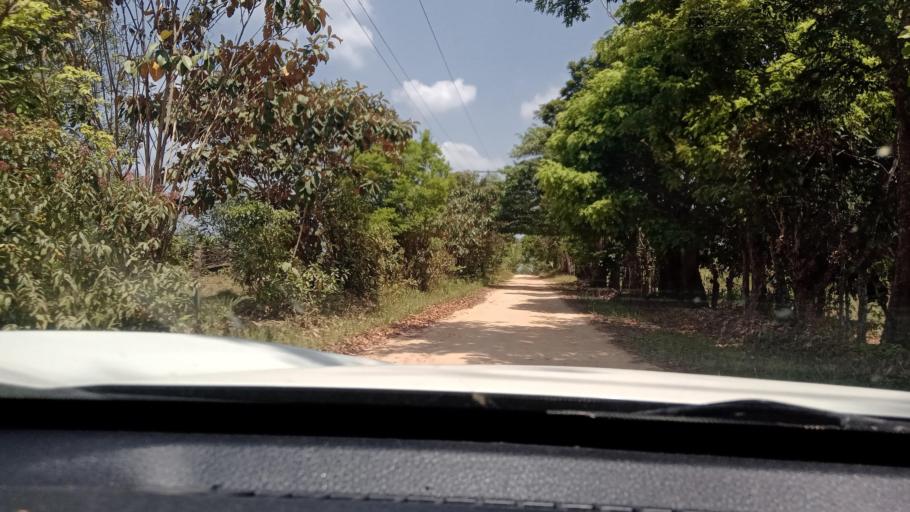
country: MX
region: Veracruz
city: Las Choapas
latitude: 17.9445
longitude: -94.1250
